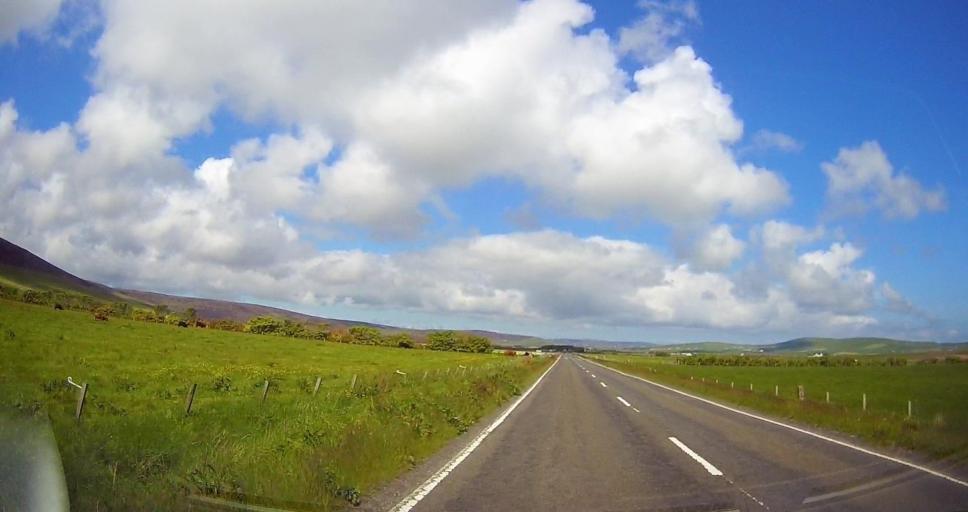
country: GB
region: Scotland
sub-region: Orkney Islands
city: Orkney
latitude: 59.0344
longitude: -3.0902
